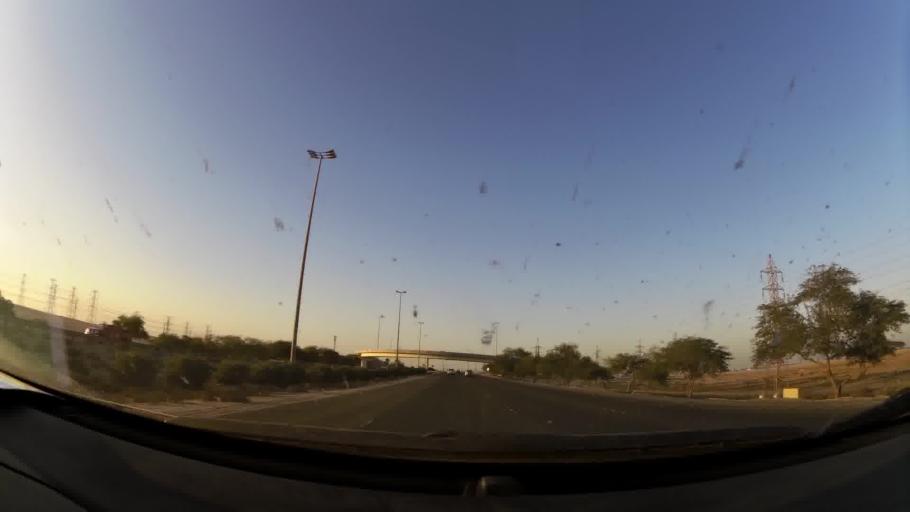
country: KW
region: Al Ahmadi
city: Al Fahahil
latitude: 28.8611
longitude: 48.2386
